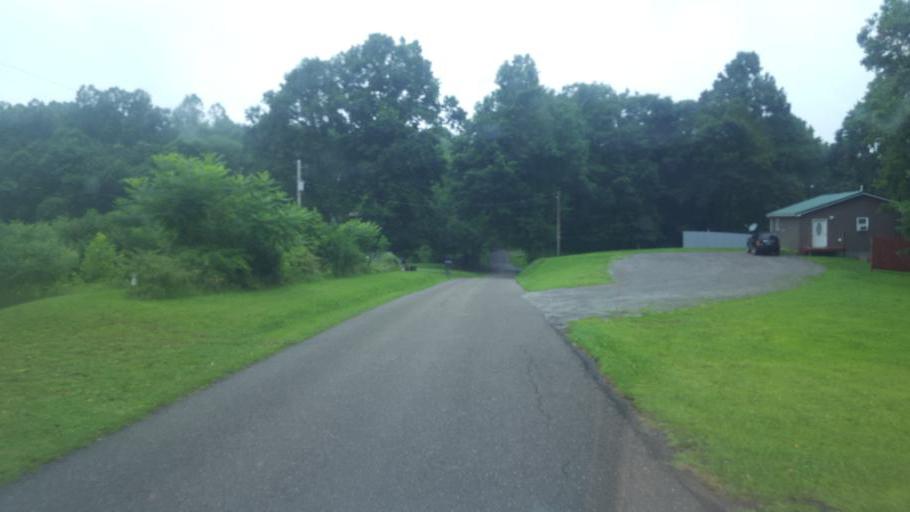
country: US
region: Ohio
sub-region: Columbiana County
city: Salineville
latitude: 40.5541
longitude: -80.8357
